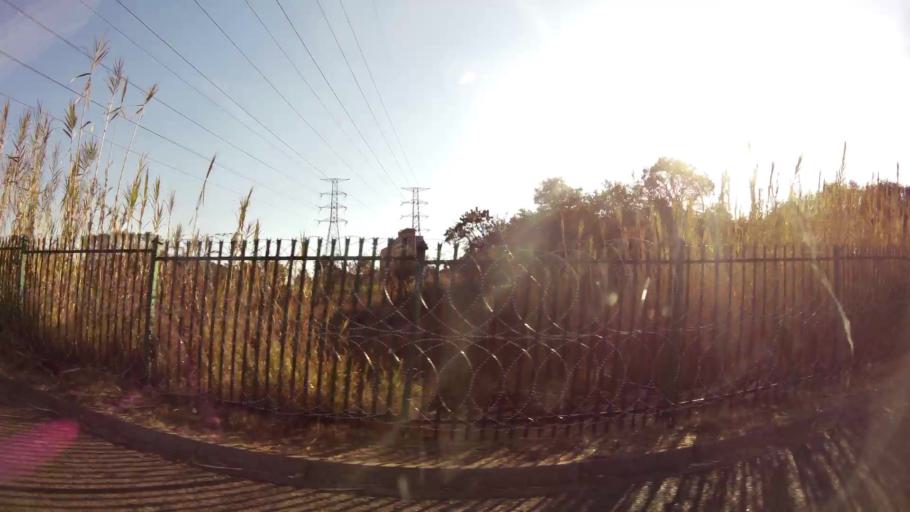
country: ZA
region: Gauteng
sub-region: City of Tshwane Metropolitan Municipality
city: Pretoria
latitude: -25.7592
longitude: 28.1331
